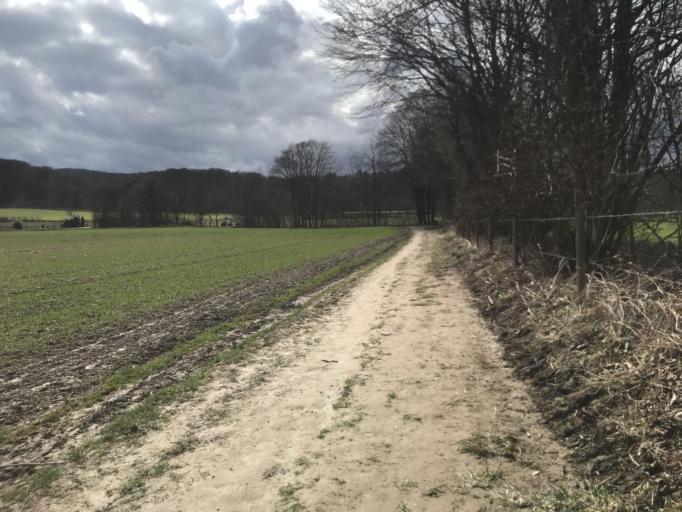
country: DE
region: Rheinland-Pfalz
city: Wassenach
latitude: 50.4015
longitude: 7.2678
